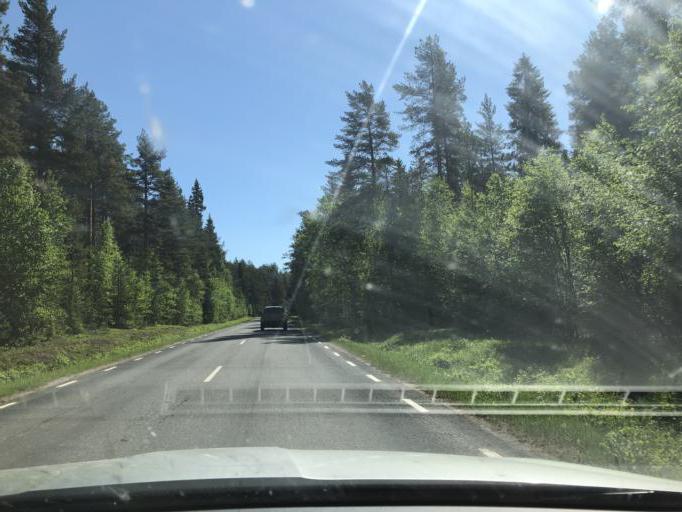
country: SE
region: Norrbotten
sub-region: Lulea Kommun
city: Gammelstad
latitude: 65.6559
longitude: 22.0080
